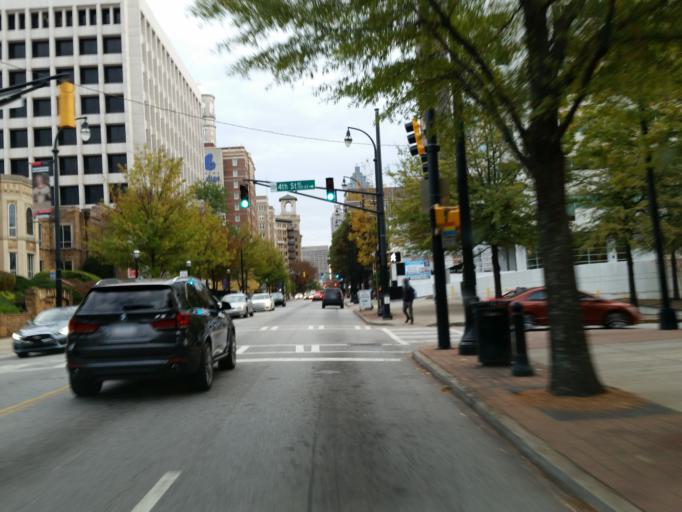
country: US
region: Georgia
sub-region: Fulton County
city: Atlanta
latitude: 33.7751
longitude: -84.3847
